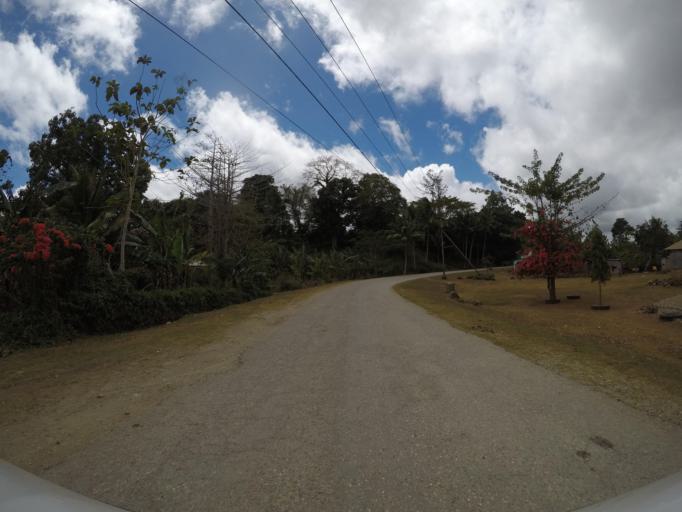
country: TL
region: Lautem
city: Lospalos
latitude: -8.4414
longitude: 126.9654
